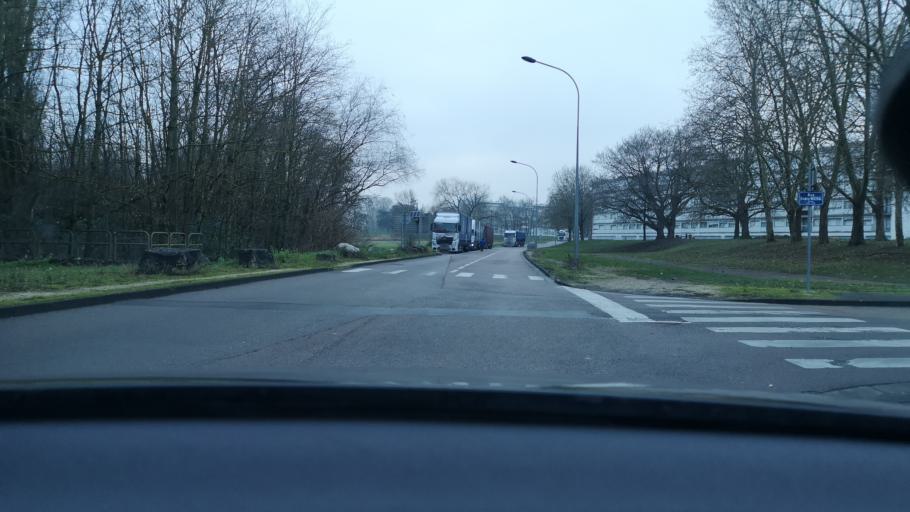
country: FR
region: Bourgogne
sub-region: Departement de Saone-et-Loire
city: Champforgeuil
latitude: 46.8029
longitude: 4.8421
